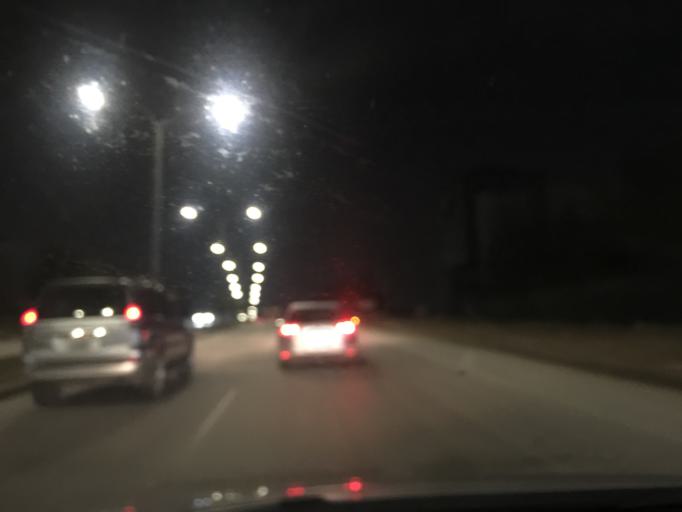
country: JO
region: Amman
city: Umm as Summaq
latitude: 31.8735
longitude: 35.8381
